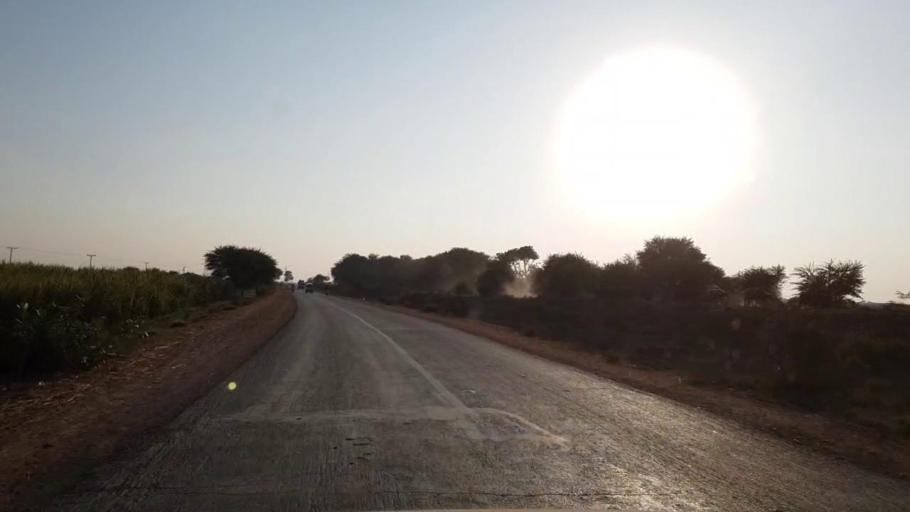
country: PK
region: Sindh
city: Daro Mehar
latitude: 24.6563
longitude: 68.1301
